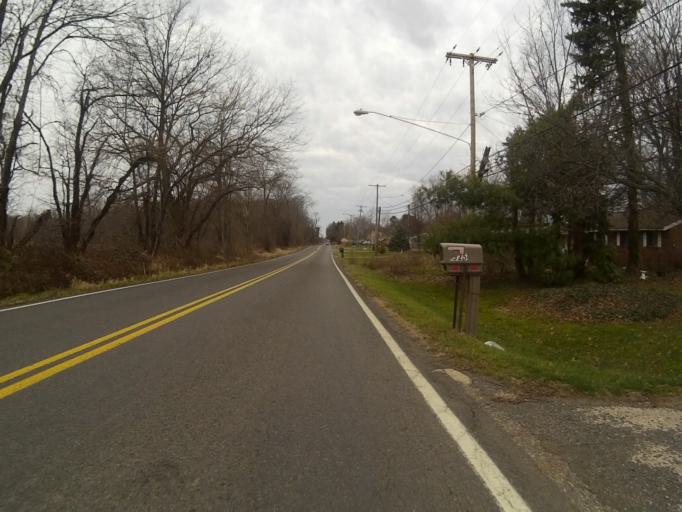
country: US
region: Ohio
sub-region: Portage County
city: Brimfield
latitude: 41.0828
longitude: -81.3382
